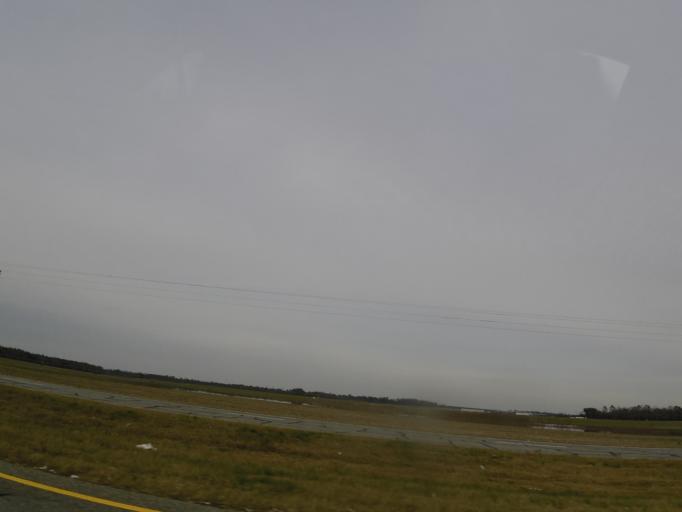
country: US
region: Georgia
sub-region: Decatur County
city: Bainbridge
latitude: 30.9352
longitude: -84.6544
